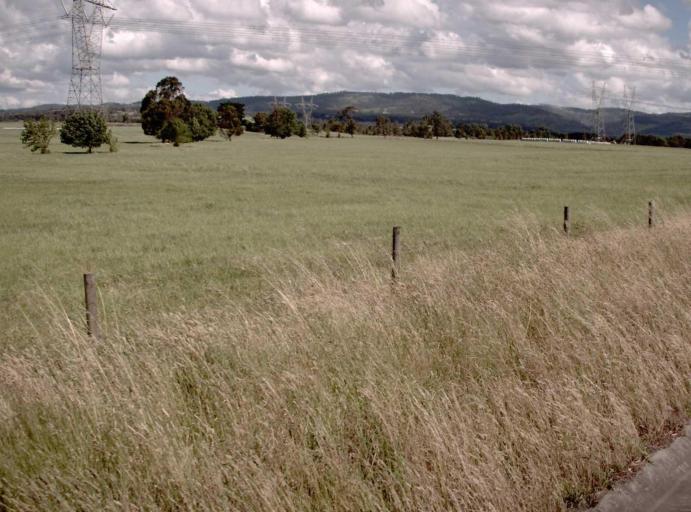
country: AU
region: Victoria
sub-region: Latrobe
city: Morwell
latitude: -38.2790
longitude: 146.4320
